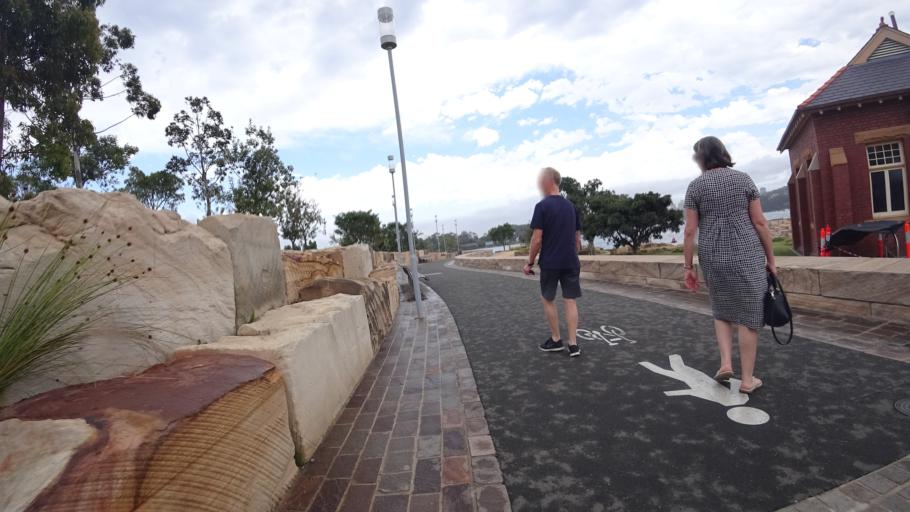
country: AU
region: New South Wales
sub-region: Leichhardt
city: Balmain East
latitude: -33.8560
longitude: 151.2020
